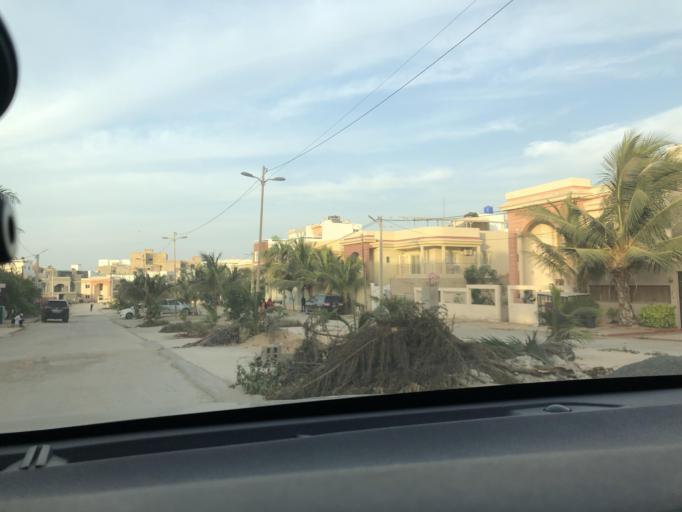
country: SN
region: Dakar
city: Mermoz Boabab
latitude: 14.7309
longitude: -17.5027
